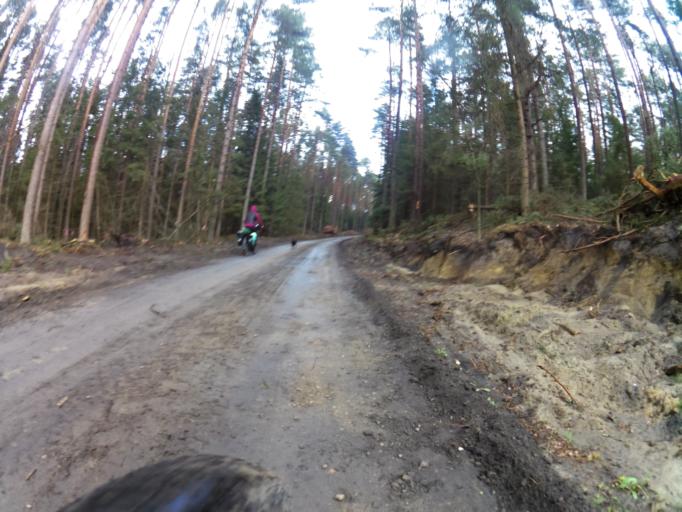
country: PL
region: Pomeranian Voivodeship
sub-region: Powiat slupski
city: Kepice
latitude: 54.2857
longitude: 16.8292
